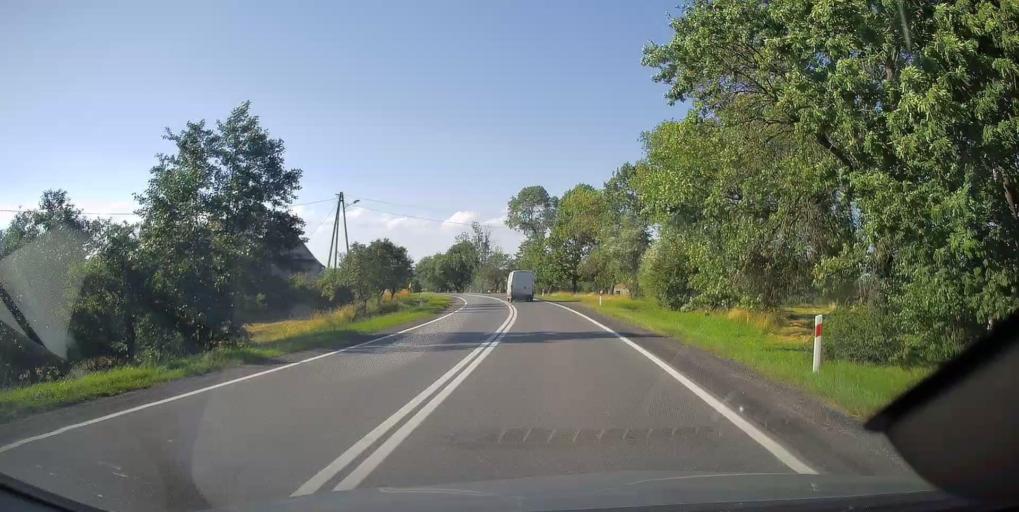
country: PL
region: Lesser Poland Voivodeship
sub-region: Powiat brzeski
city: Gnojnik
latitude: 49.8781
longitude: 20.6181
